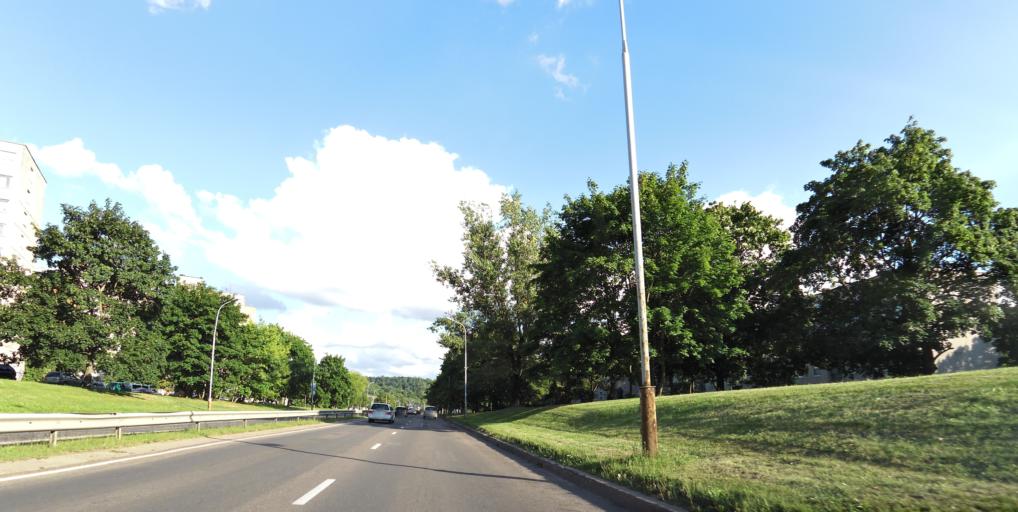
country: LT
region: Vilnius County
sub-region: Vilnius
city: Vilnius
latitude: 54.6990
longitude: 25.2946
